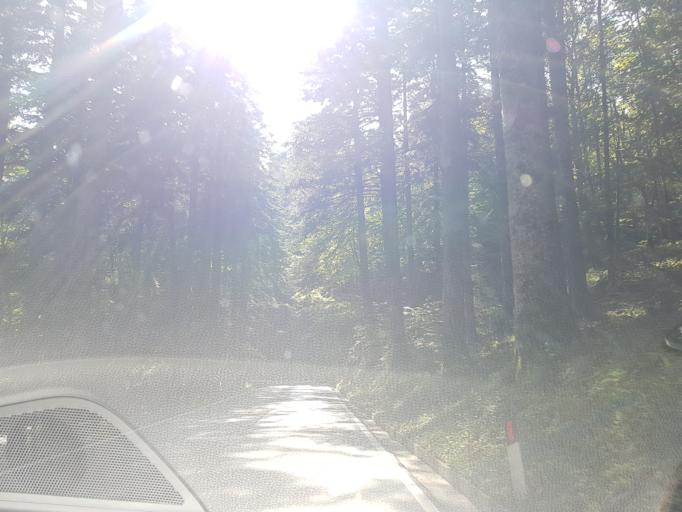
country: IT
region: Tuscany
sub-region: Province of Arezzo
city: Soci
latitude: 43.7966
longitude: 11.8893
